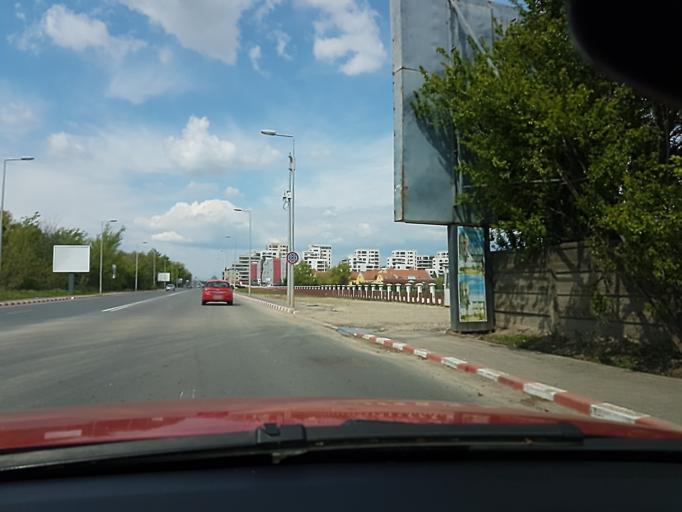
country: RO
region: Ilfov
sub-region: Comuna Tunari
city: Tunari
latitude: 44.5277
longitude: 26.1434
